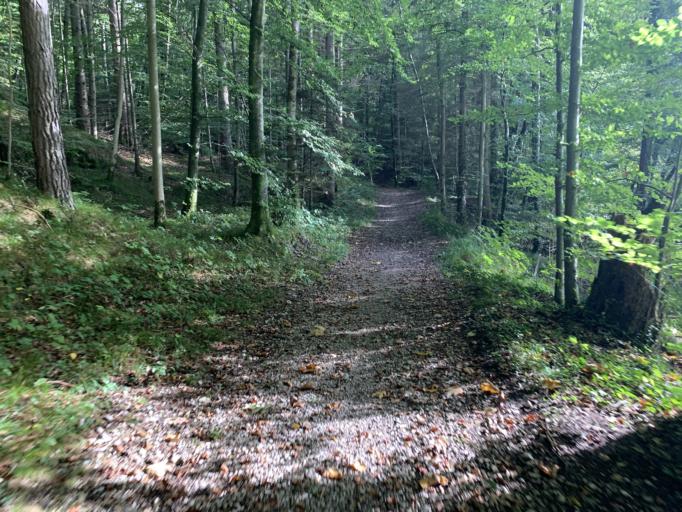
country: DE
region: Bavaria
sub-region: Upper Bavaria
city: Baierbrunn
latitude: 48.0243
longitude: 11.4974
